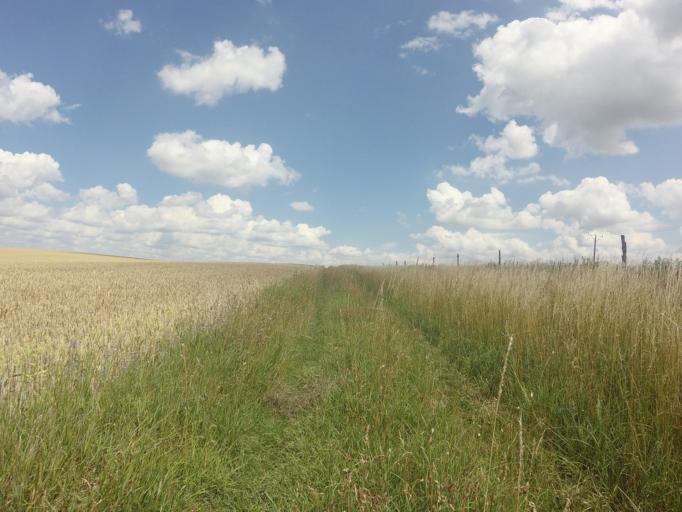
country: PL
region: West Pomeranian Voivodeship
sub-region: Powiat choszczenski
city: Choszczno
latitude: 53.2050
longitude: 15.4904
